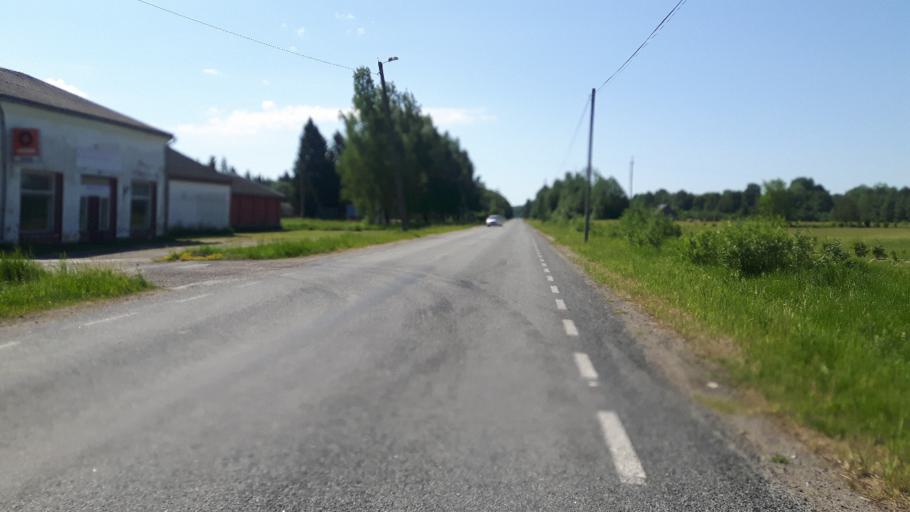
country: EE
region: Paernumaa
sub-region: Vaendra vald (alev)
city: Vandra
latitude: 58.6447
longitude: 25.0282
